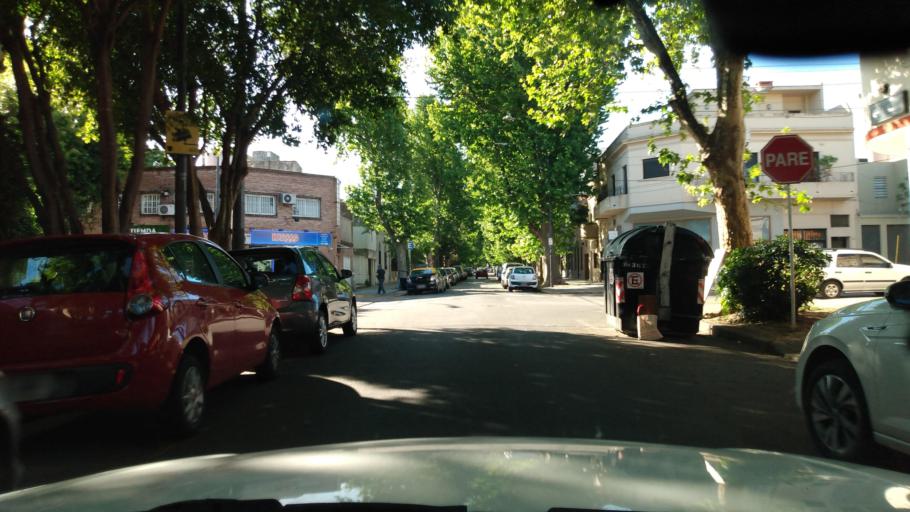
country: AR
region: Buenos Aires F.D.
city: Villa Santa Rita
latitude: -34.5830
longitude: -58.4849
